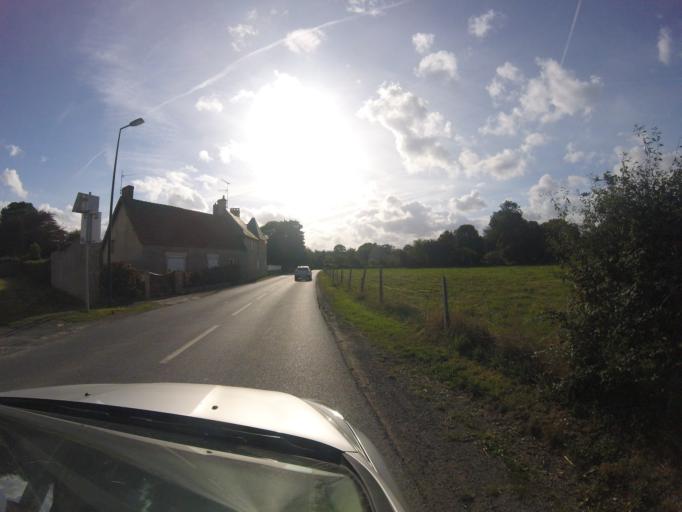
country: FR
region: Lower Normandy
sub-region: Departement du Calvados
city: Port-en-Bessin-Huppain
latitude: 49.3473
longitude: -0.8512
